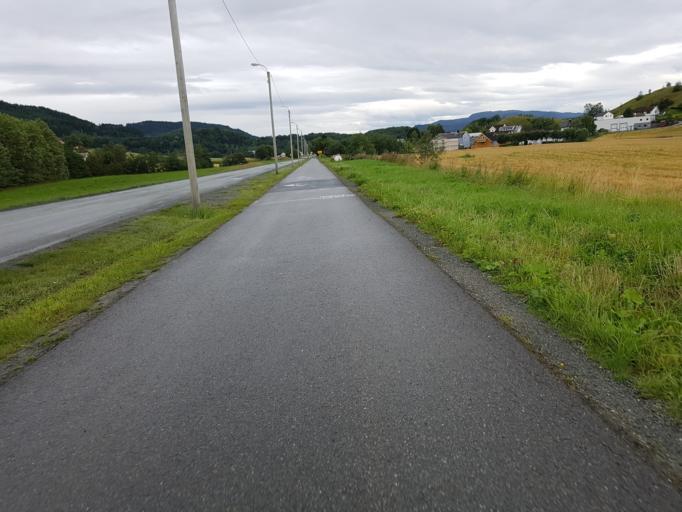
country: NO
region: Sor-Trondelag
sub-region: Trondheim
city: Trondheim
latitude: 63.3863
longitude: 10.4346
